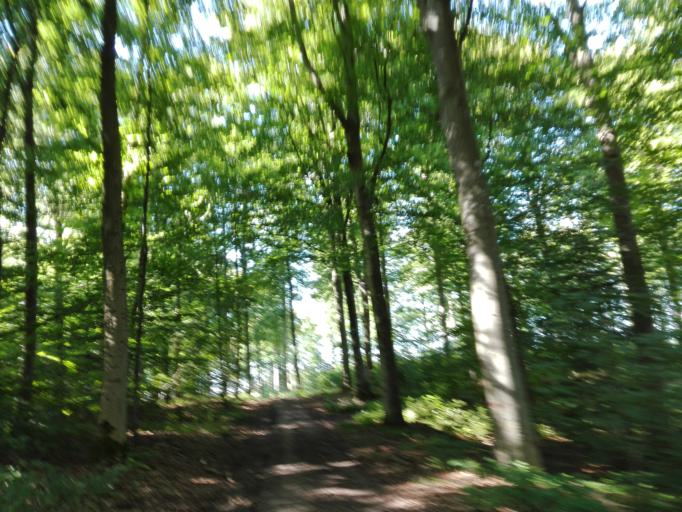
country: DK
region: Central Jutland
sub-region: Odder Kommune
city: Odder
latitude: 55.9704
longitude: 10.1247
